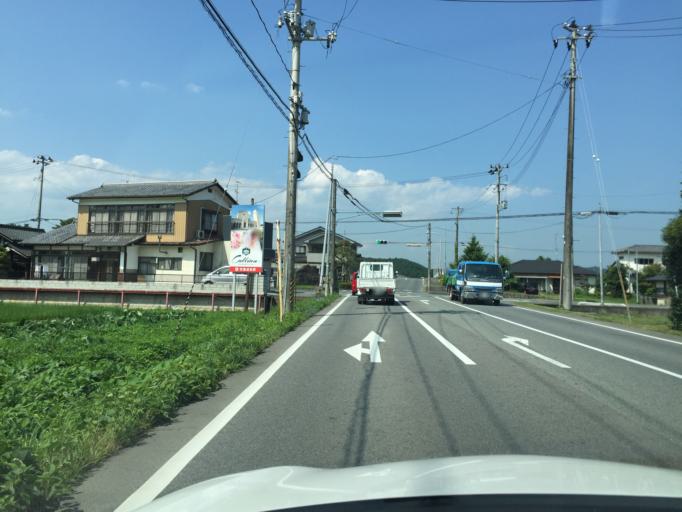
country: JP
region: Ibaraki
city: Kitaibaraki
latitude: 36.9185
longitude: 140.7467
